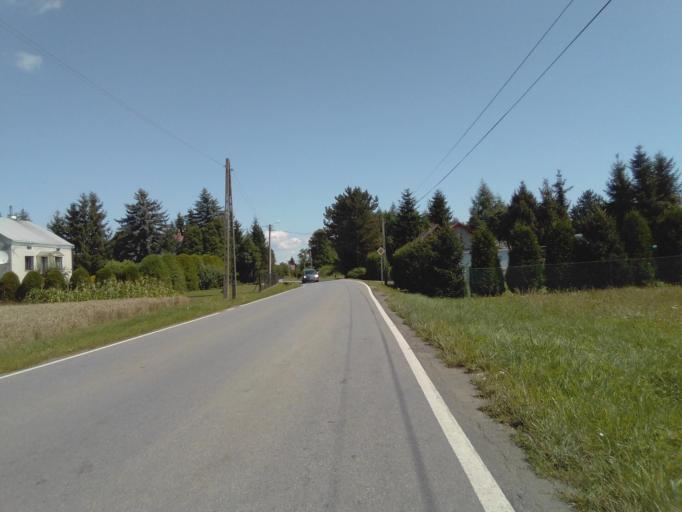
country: PL
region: Subcarpathian Voivodeship
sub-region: Powiat krosnienski
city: Jedlicze
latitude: 49.6994
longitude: 21.6206
